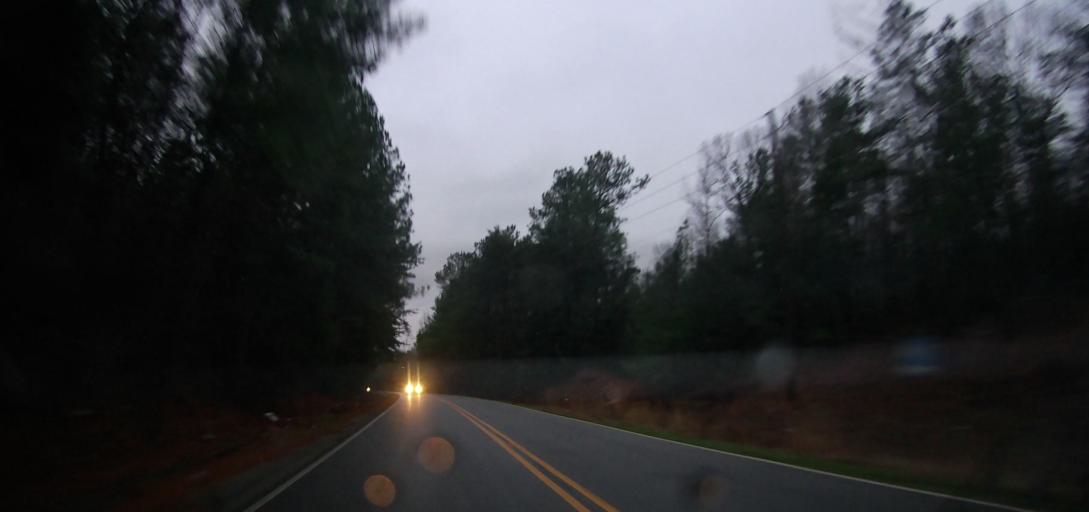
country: US
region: Alabama
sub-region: Tuscaloosa County
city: Vance
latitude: 33.1289
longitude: -87.2296
